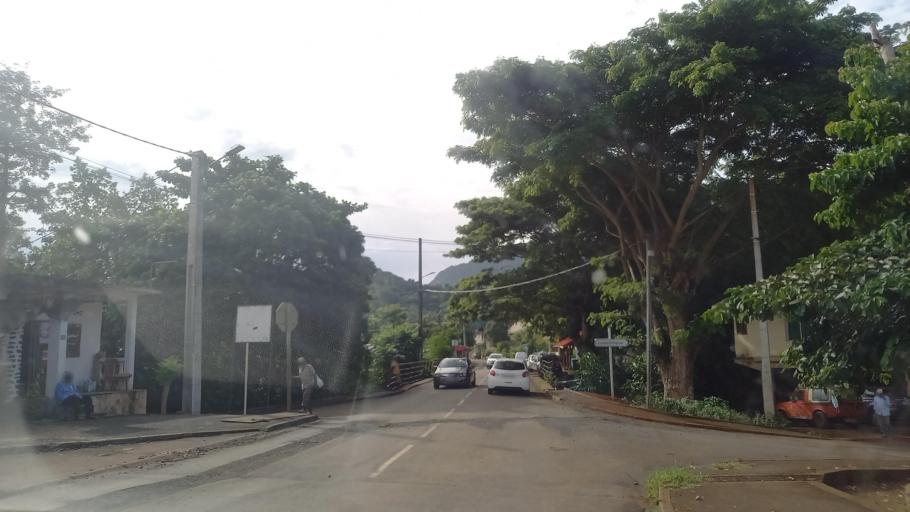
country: YT
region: Chirongui
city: Chirongui
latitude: -12.8941
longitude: 45.1420
